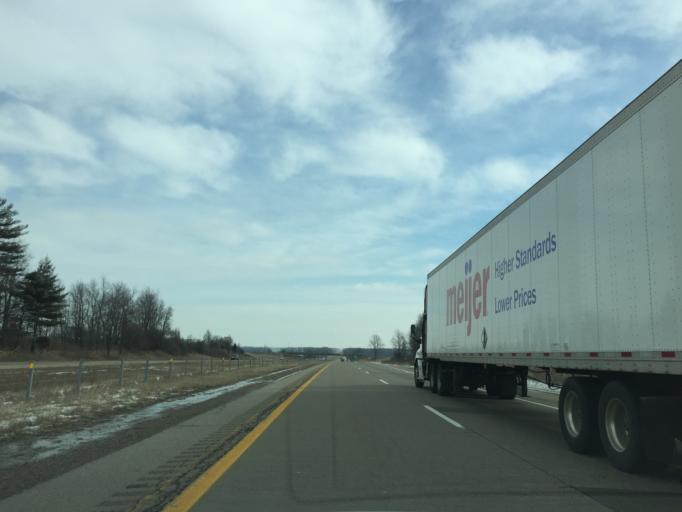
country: US
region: Michigan
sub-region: Ionia County
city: Saranac
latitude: 42.8793
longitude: -85.2521
